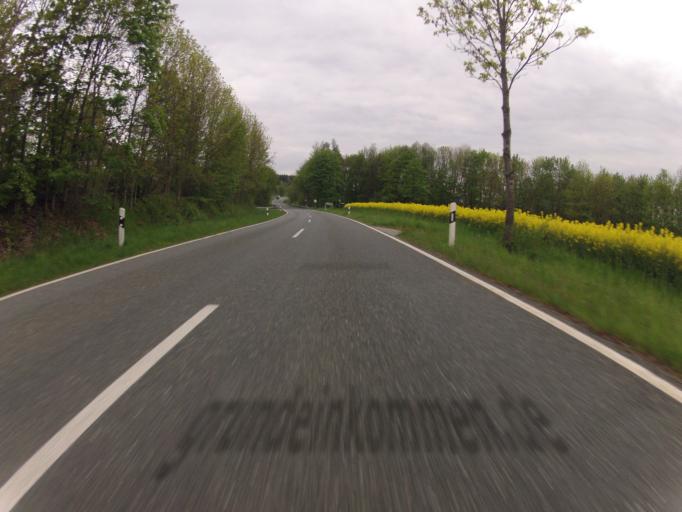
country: DE
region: Bavaria
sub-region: Upper Franconia
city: Sparneck
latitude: 50.1497
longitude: 11.8425
